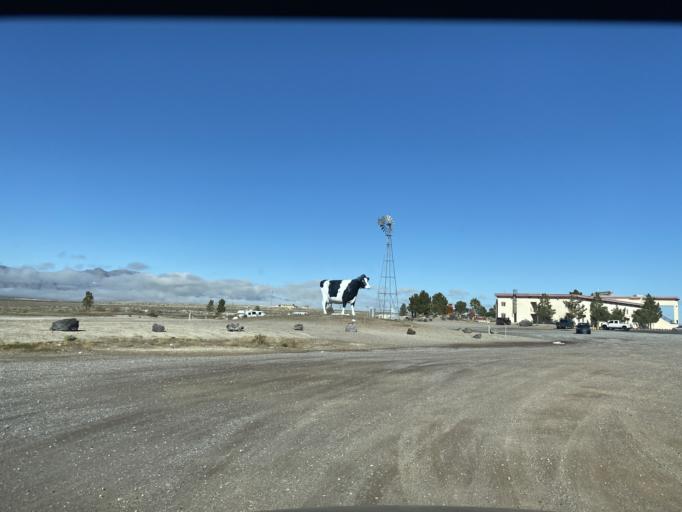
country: US
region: Nevada
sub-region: Nye County
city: Pahrump
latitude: 36.4110
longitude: -116.4227
